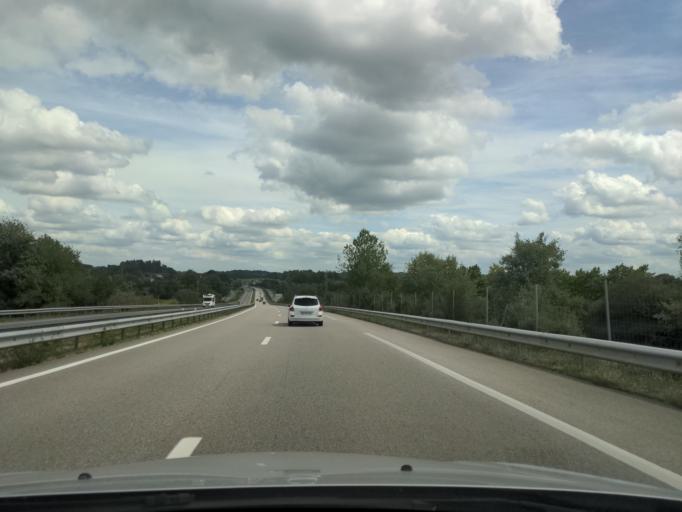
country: FR
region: Limousin
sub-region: Departement de la Creuse
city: La Souterraine
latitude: 46.2231
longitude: 1.4951
